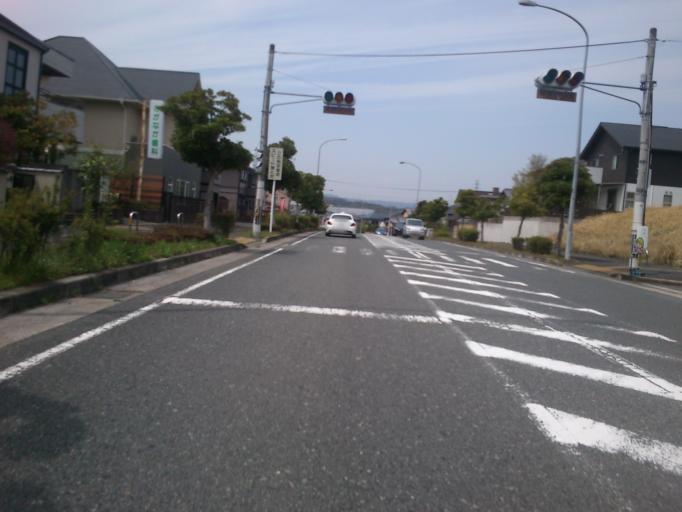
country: JP
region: Nara
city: Nara-shi
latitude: 34.7268
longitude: 135.7954
